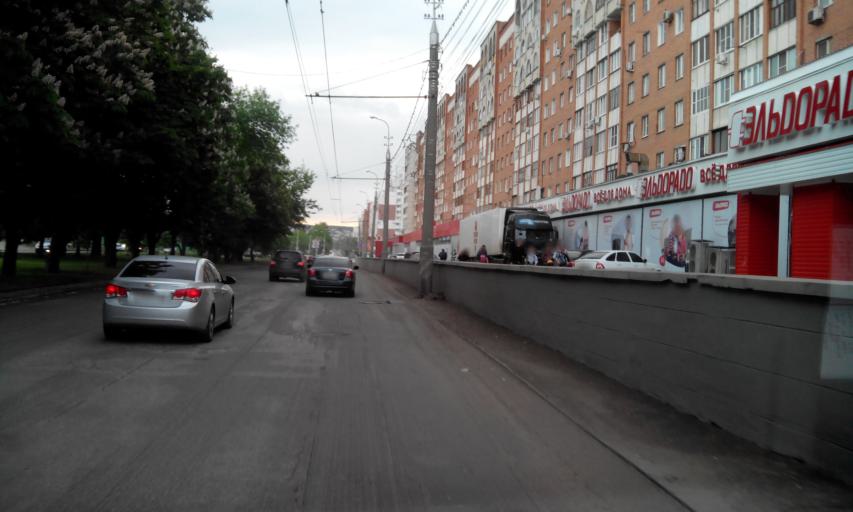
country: RU
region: Penza
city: Penza
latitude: 53.1969
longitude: 45.0032
